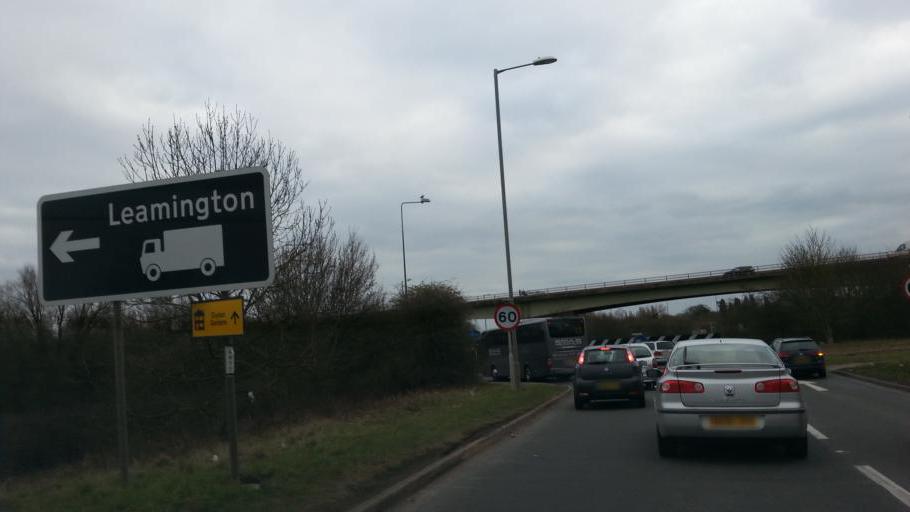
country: GB
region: England
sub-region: Solihull
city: Hampton in Arden
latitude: 52.4467
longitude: -1.6875
